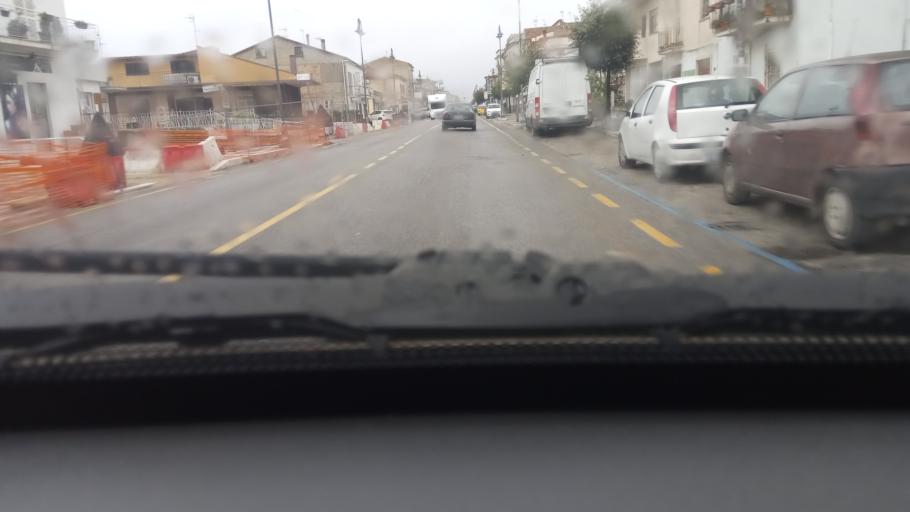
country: IT
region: Latium
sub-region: Provincia di Latina
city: Minturno
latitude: 41.2541
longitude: 13.7182
